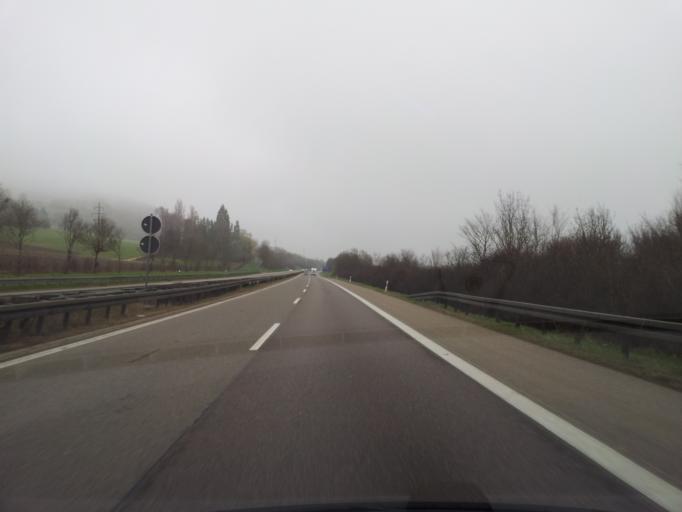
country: DE
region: Baden-Wuerttemberg
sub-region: Freiburg Region
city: Singen
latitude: 47.7763
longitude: 8.8180
